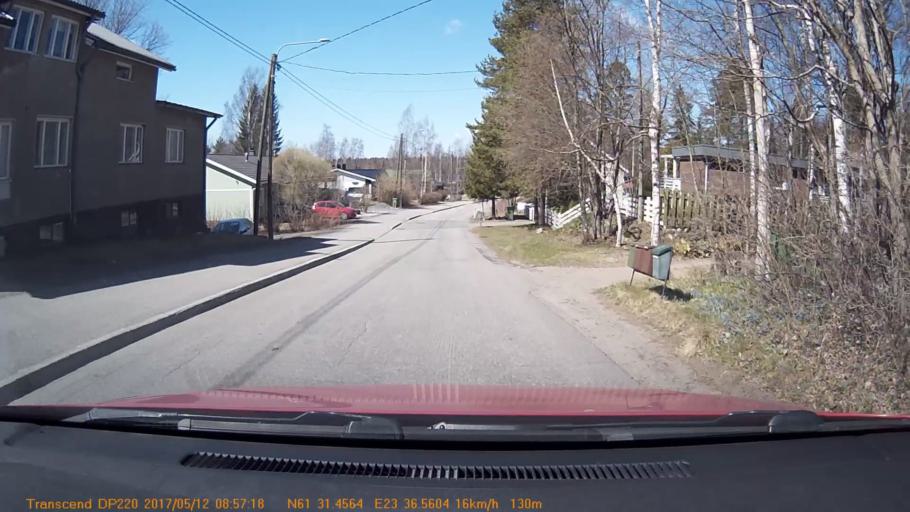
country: FI
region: Pirkanmaa
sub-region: Tampere
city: Yloejaervi
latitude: 61.5243
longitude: 23.6094
